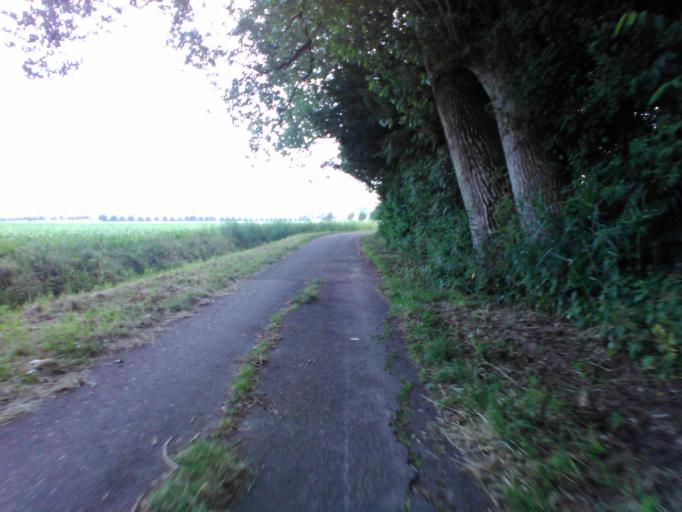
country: NL
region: North Brabant
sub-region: Gemeente Woudrichem
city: Woudrichem
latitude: 51.7833
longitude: 4.9927
